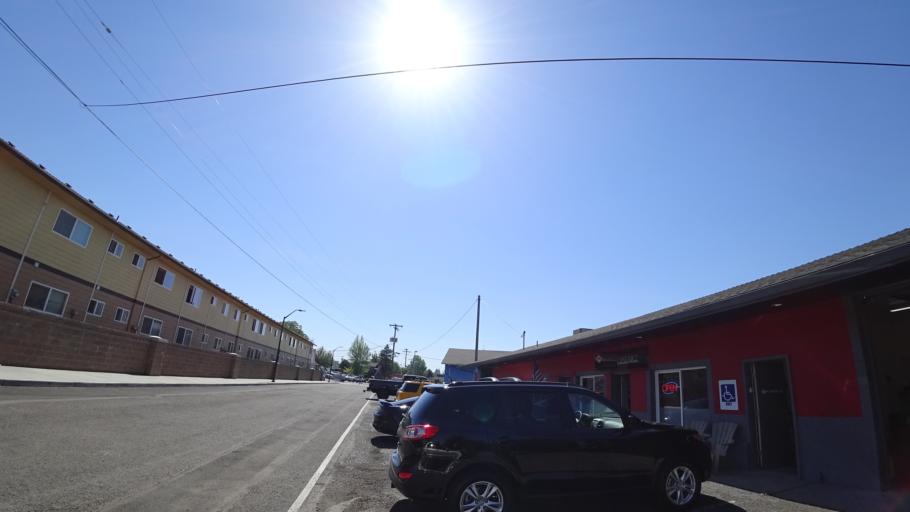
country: US
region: Oregon
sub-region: Washington County
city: Beaverton
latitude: 45.4901
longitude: -122.8024
